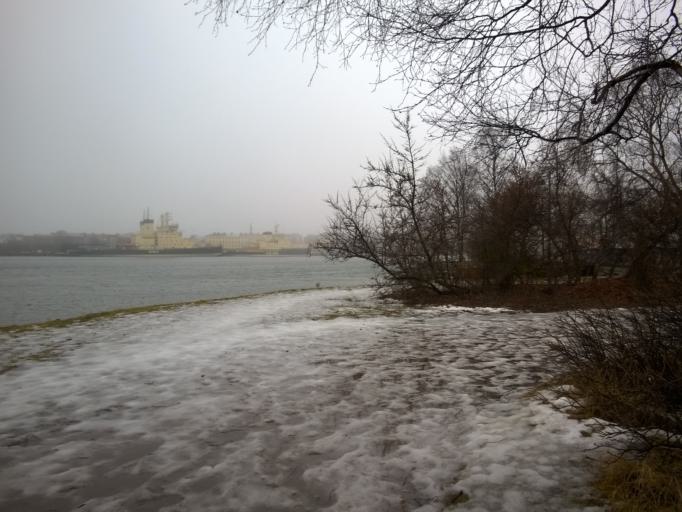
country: FI
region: Uusimaa
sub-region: Helsinki
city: Helsinki
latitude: 60.1734
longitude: 24.9701
